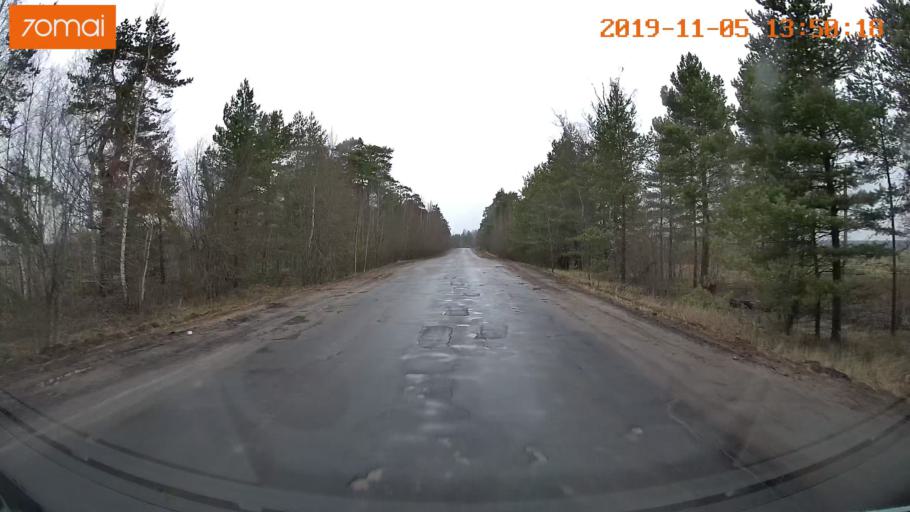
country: RU
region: Ivanovo
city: Kaminskiy
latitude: 57.0183
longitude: 41.4086
